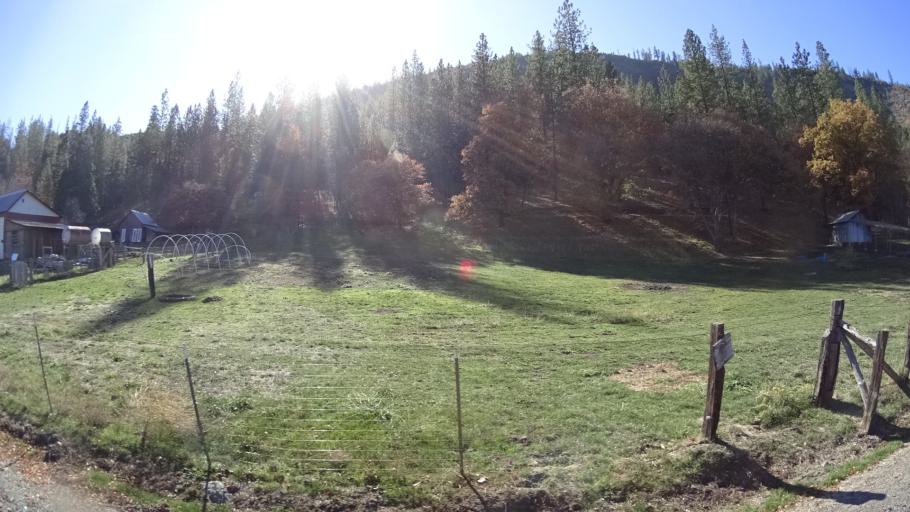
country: US
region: California
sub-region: Siskiyou County
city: Yreka
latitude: 41.8347
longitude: -122.8617
